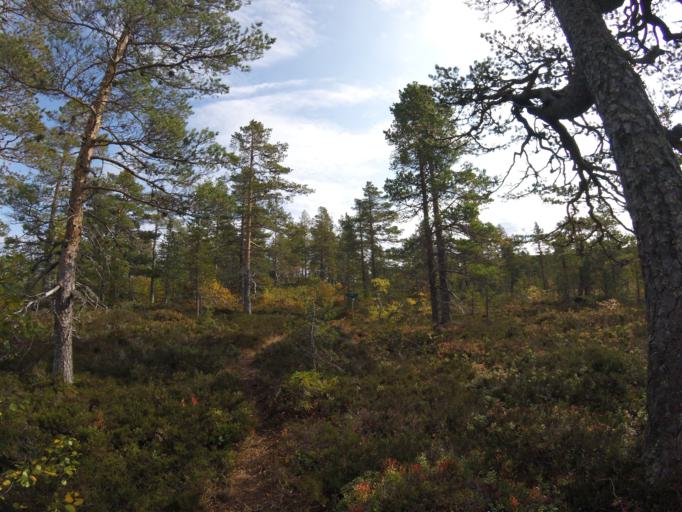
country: NO
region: Buskerud
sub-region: Rollag
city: Rollag
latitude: 59.8162
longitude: 9.3520
